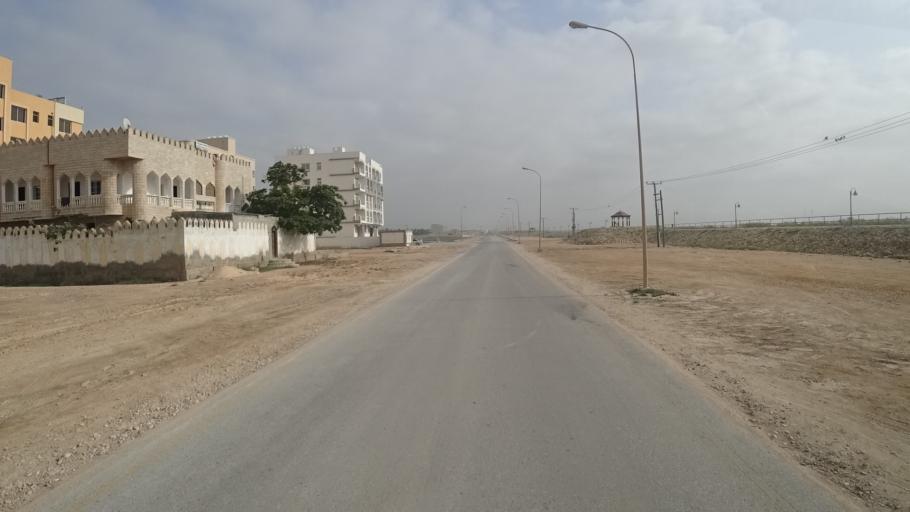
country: OM
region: Zufar
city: Salalah
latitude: 17.0150
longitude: 54.1750
